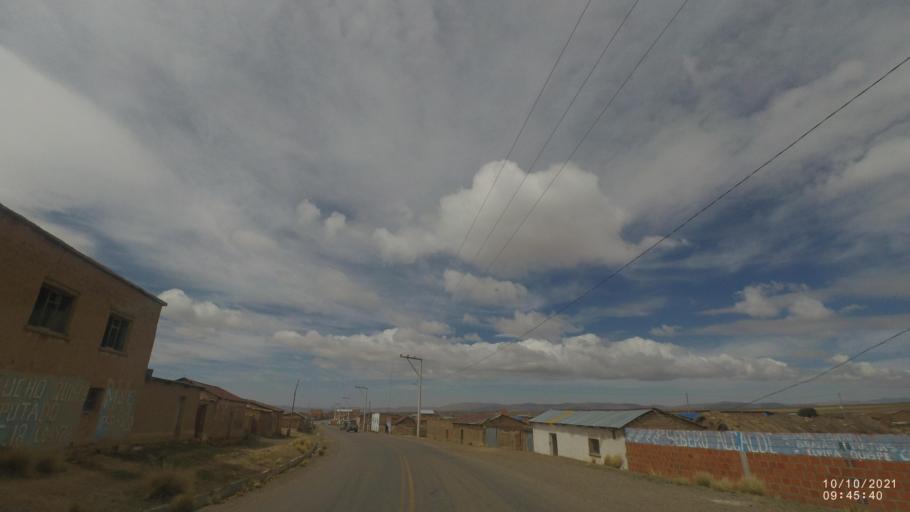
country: BO
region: La Paz
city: Quime
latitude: -17.1734
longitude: -67.3372
